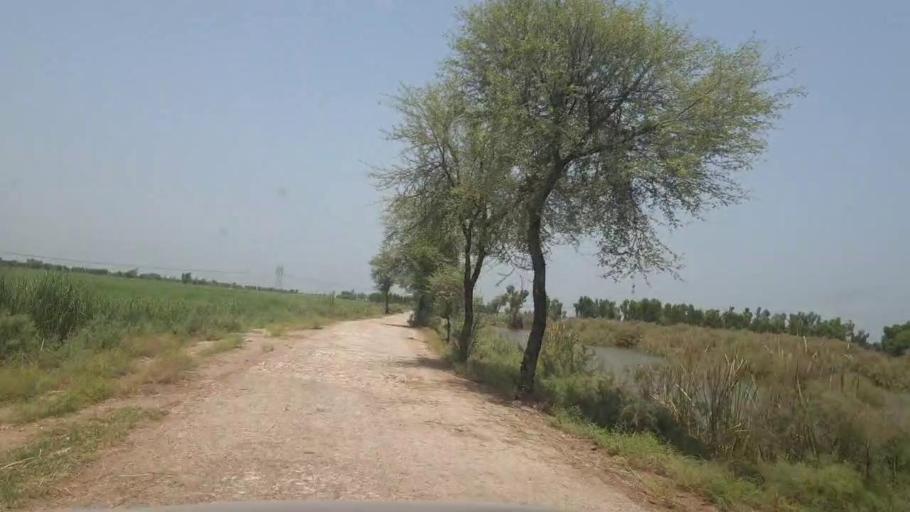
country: PK
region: Sindh
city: Lakhi
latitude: 27.8570
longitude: 68.6245
